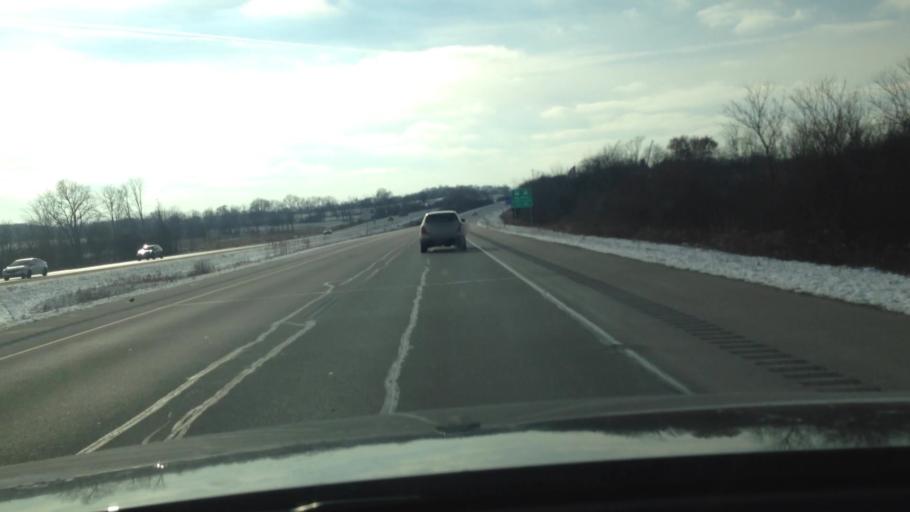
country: US
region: Wisconsin
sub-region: Waukesha County
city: Big Bend
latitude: 42.9174
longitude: -88.2020
